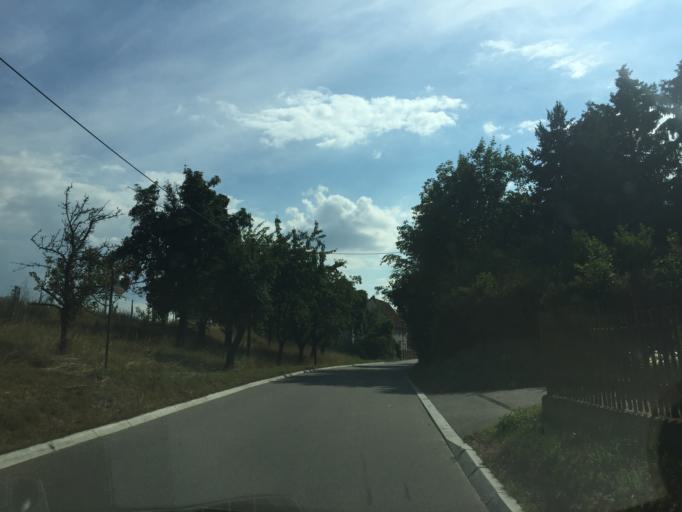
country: DE
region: Thuringia
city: Vollmershain
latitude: 50.8723
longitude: 12.3083
